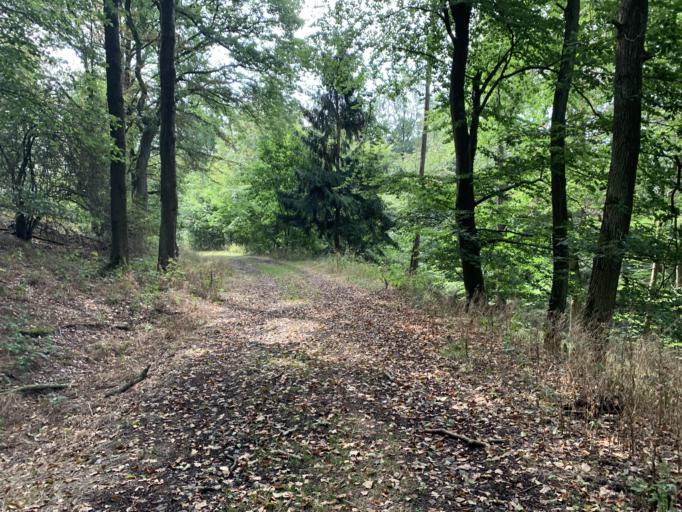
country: DE
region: Rheinland-Pfalz
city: Rettert
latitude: 50.2229
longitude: 7.9389
